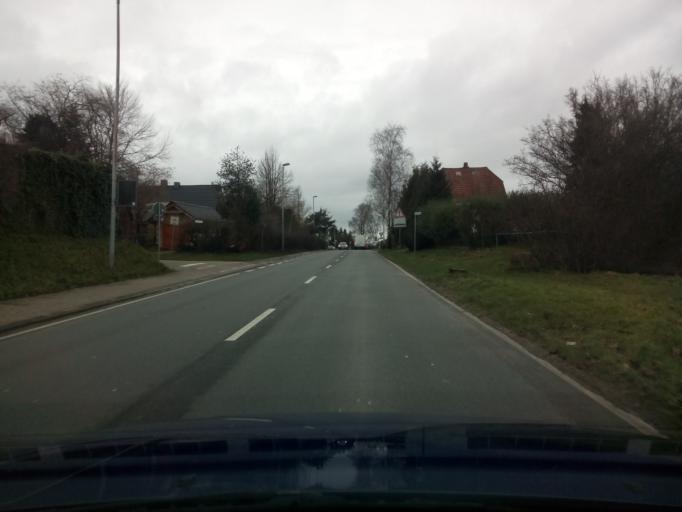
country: DE
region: Lower Saxony
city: Ritterhude
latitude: 53.1931
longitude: 8.7532
